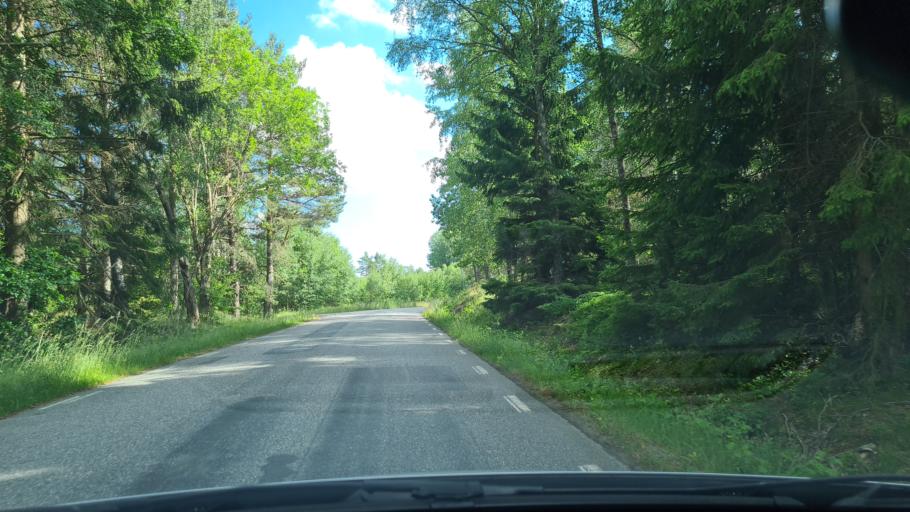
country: SE
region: Stockholm
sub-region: Varmdo Kommun
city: Mortnas
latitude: 59.3980
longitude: 18.4650
